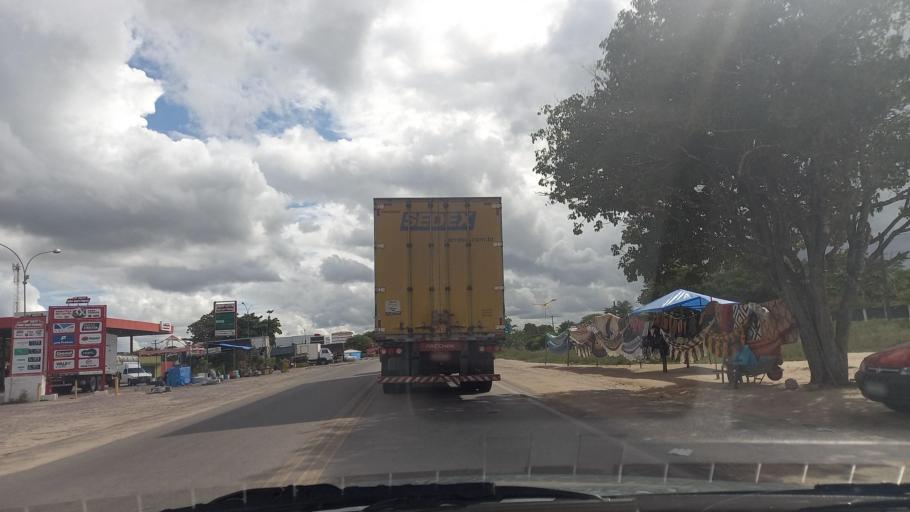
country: BR
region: Pernambuco
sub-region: Lajedo
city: Lajedo
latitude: -8.6581
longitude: -36.3291
